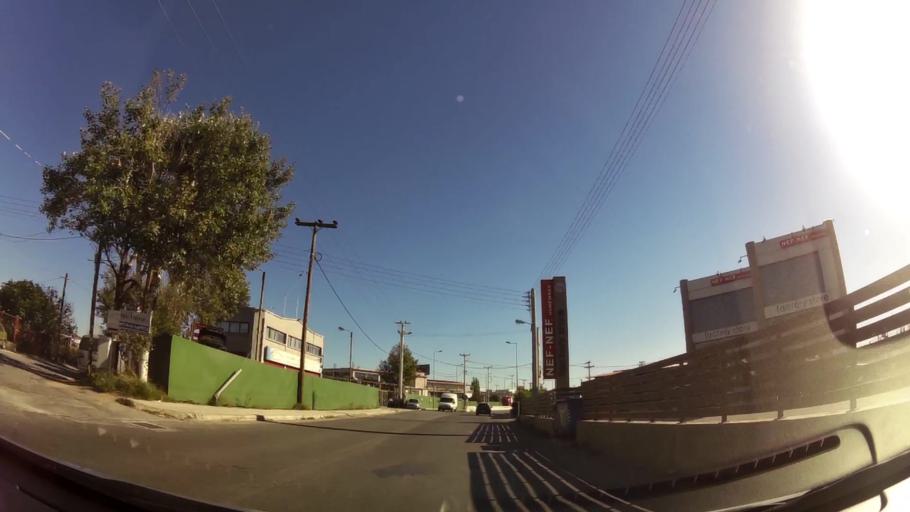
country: GR
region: Attica
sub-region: Nomarchia Athinas
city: Metamorfosi
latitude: 38.0909
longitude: 23.7607
